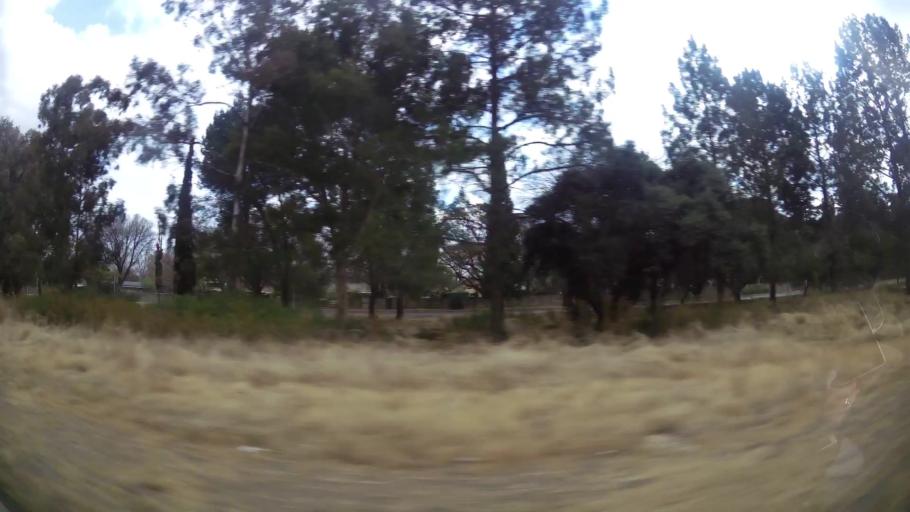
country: ZA
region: Orange Free State
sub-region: Fezile Dabi District Municipality
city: Sasolburg
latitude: -26.8075
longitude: 27.8367
